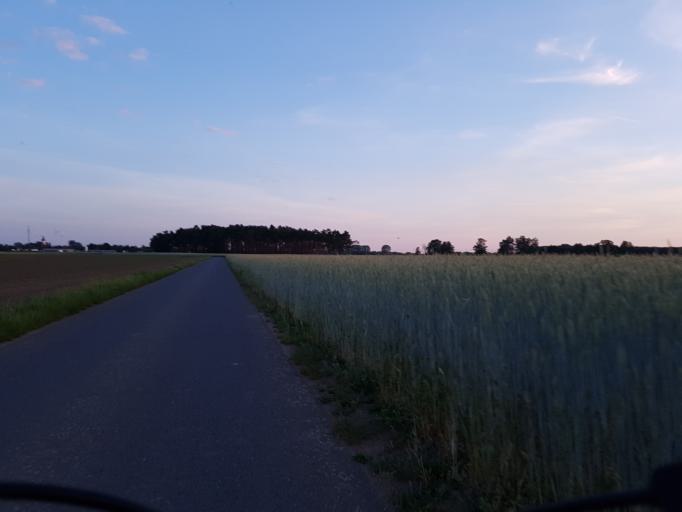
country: DE
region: Brandenburg
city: Falkenberg
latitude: 51.6063
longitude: 13.3030
